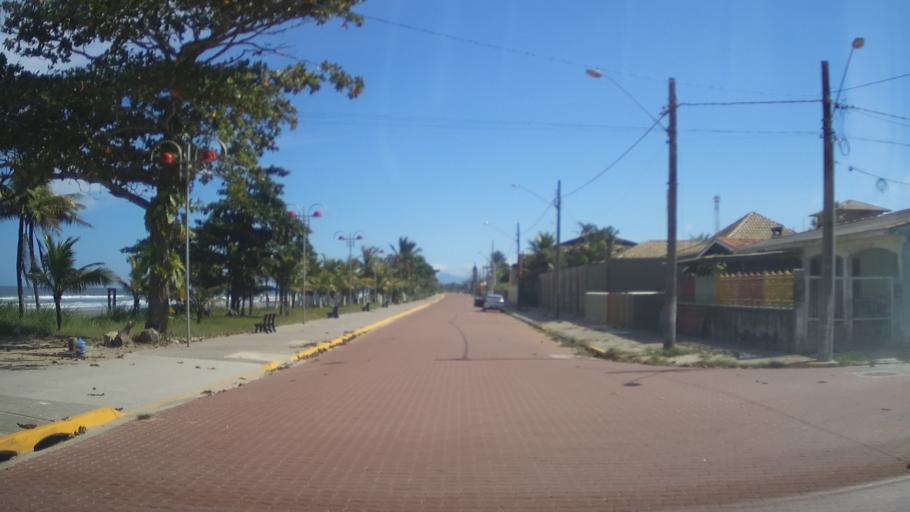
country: BR
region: Sao Paulo
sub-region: Itanhaem
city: Itanhaem
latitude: -24.1668
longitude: -46.7517
